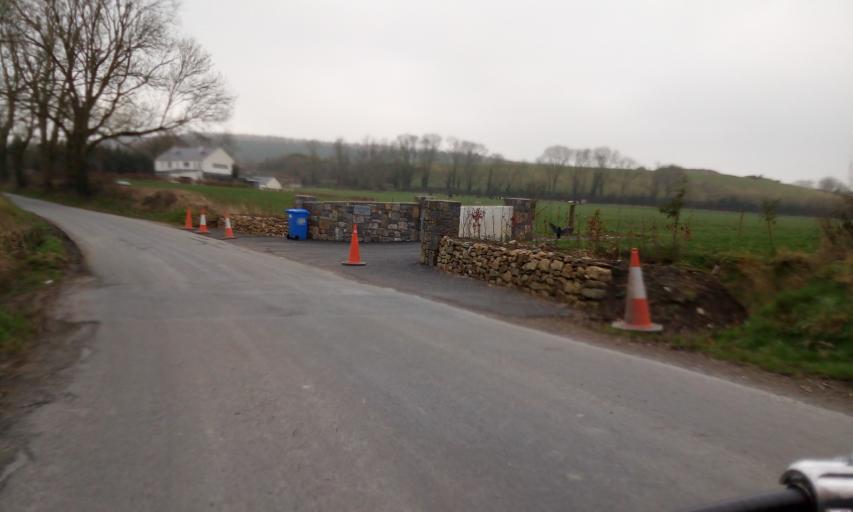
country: IE
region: Leinster
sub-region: Kilkenny
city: Kilkenny
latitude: 52.6578
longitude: -7.1453
